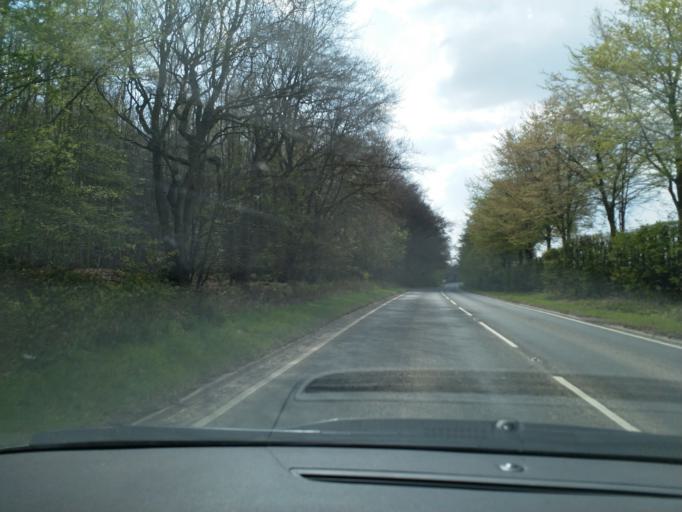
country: GB
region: England
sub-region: Warwickshire
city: Royal Leamington Spa
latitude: 52.3356
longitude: -1.4876
